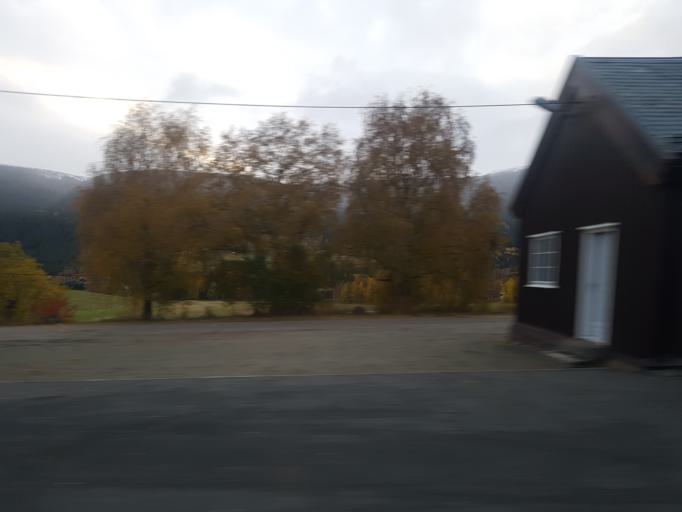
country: NO
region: Oppland
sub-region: Dovre
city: Dovre
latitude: 61.9902
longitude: 9.2484
